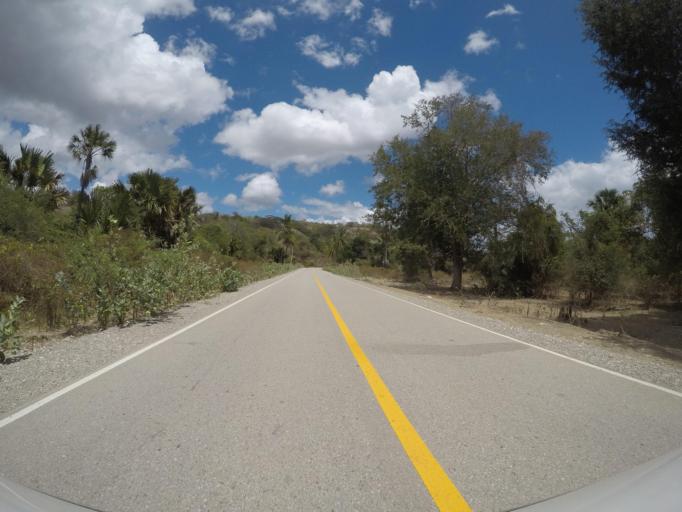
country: TL
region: Lautem
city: Lospalos
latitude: -8.4140
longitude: 126.8048
